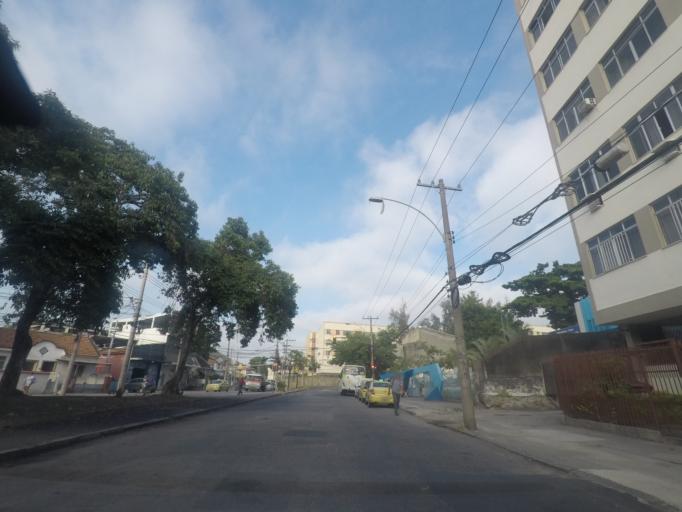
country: BR
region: Rio de Janeiro
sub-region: Duque De Caxias
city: Duque de Caxias
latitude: -22.8420
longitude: -43.2692
